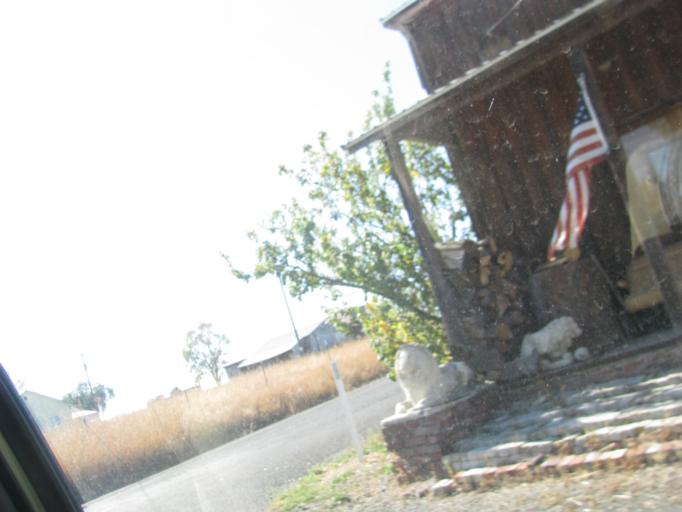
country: US
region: Washington
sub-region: Asotin County
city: Asotin
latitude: 46.1350
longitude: -117.1324
